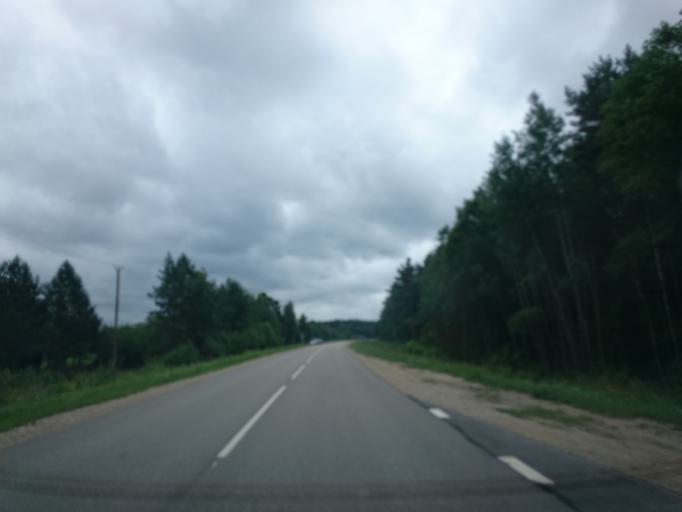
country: LV
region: Pavilostas
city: Pavilosta
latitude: 56.7723
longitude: 21.2563
